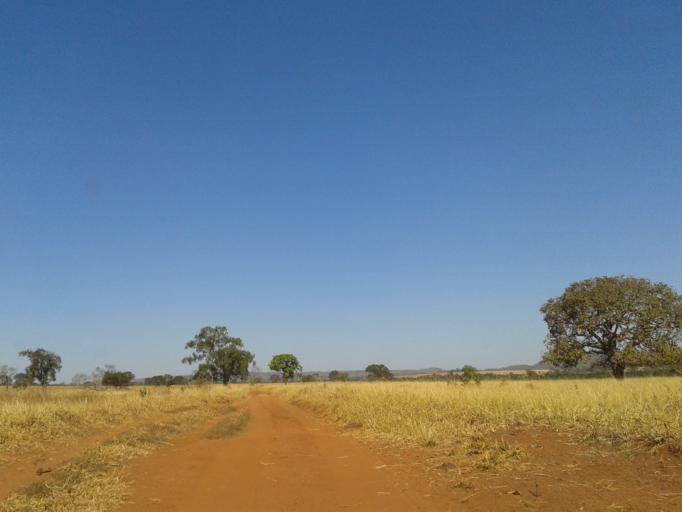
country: BR
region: Minas Gerais
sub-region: Santa Vitoria
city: Santa Vitoria
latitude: -19.1511
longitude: -50.0307
